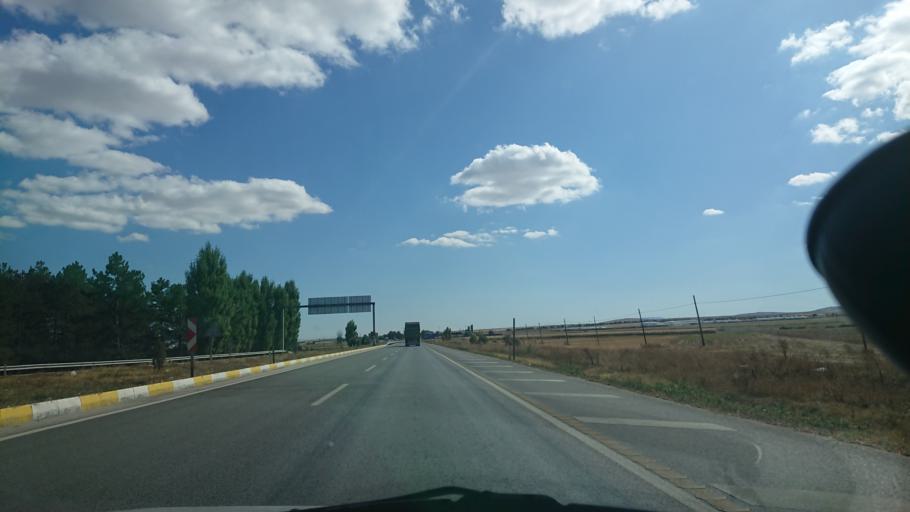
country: TR
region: Eskisehir
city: Mahmudiye
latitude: 39.5695
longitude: 30.9135
